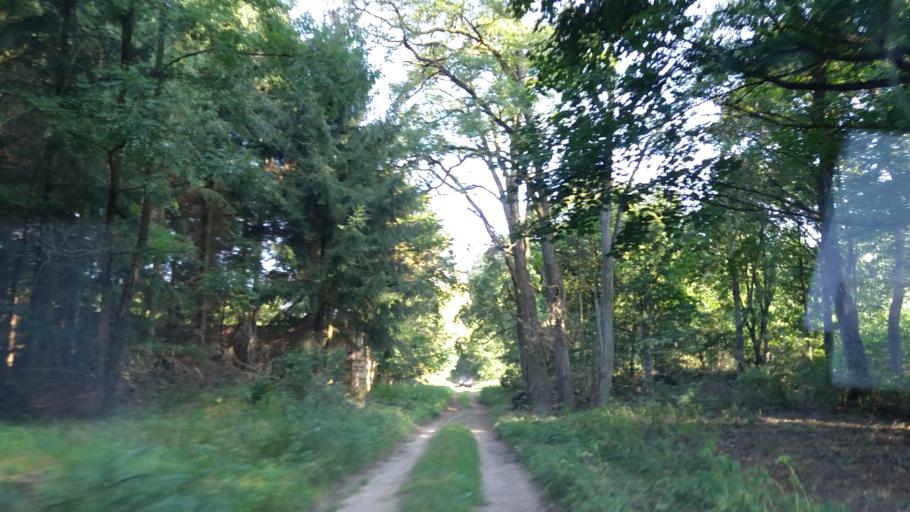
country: PL
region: West Pomeranian Voivodeship
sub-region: Powiat choszczenski
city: Recz
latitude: 53.1964
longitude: 15.5421
